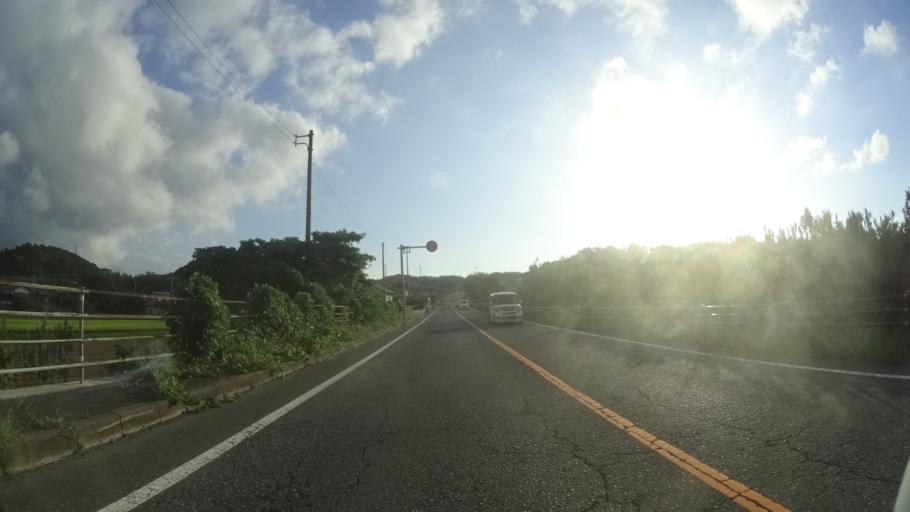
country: JP
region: Tottori
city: Yonago
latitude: 35.5195
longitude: 133.5557
